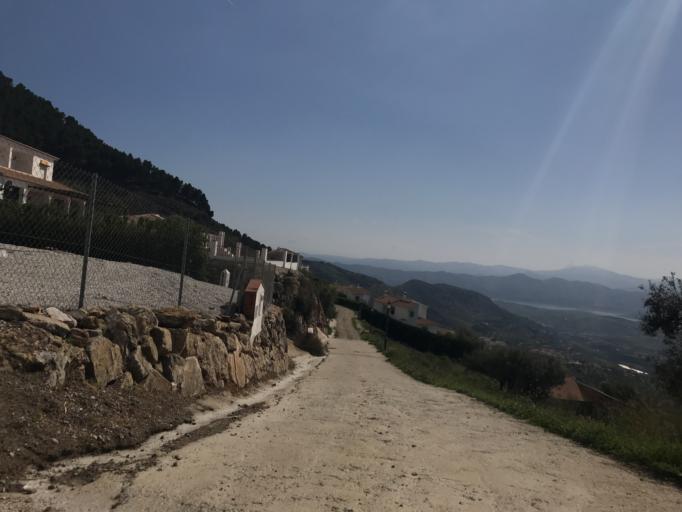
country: ES
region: Andalusia
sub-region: Provincia de Malaga
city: Alcaucin
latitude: 36.9099
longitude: -4.1089
